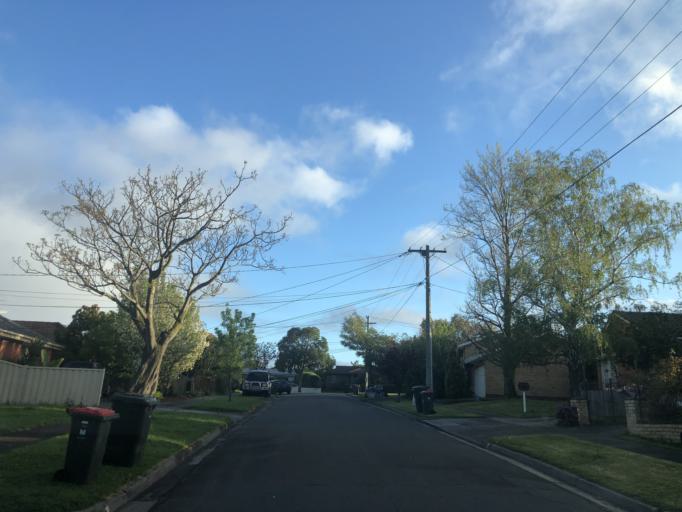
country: AU
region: Victoria
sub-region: Monash
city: Chadstone
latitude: -37.8853
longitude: 145.1066
